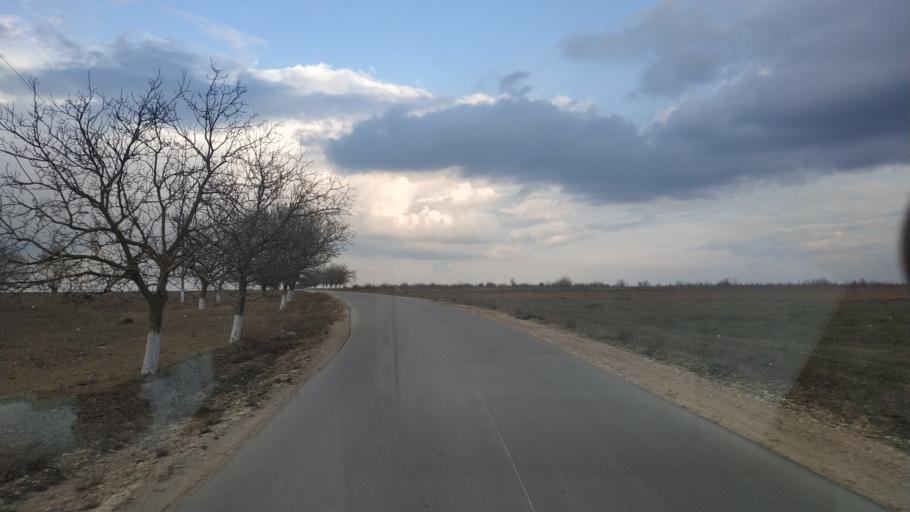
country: MD
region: Telenesti
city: Grigoriopol
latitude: 47.0228
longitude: 29.3165
